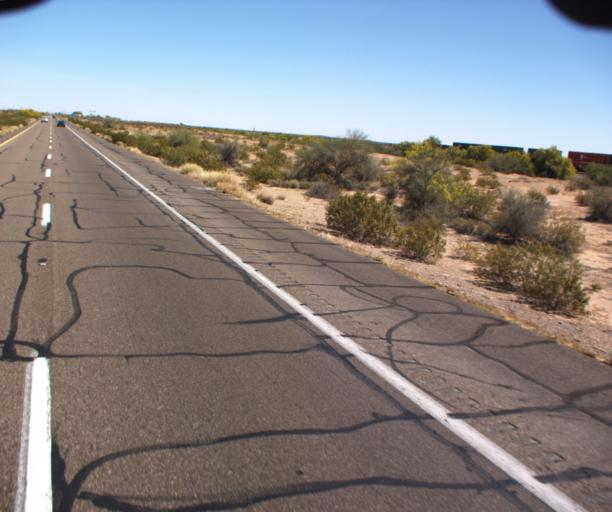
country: US
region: Arizona
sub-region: Maricopa County
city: Gila Bend
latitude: 32.8463
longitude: -113.2763
